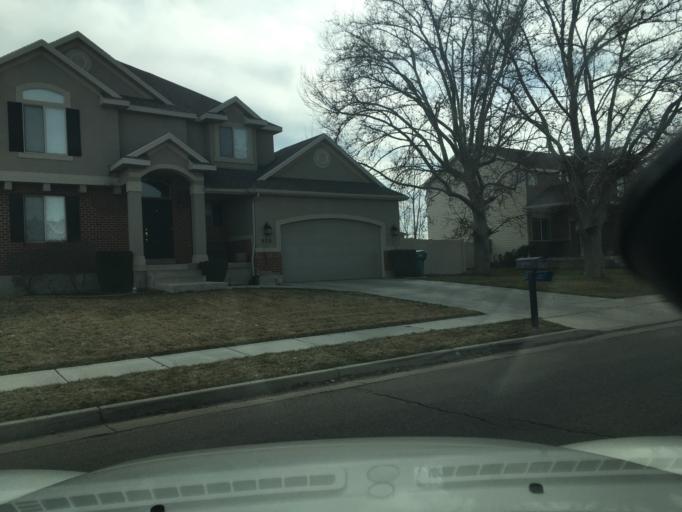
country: US
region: Utah
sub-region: Davis County
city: Clearfield
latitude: 41.0822
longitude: -112.0073
